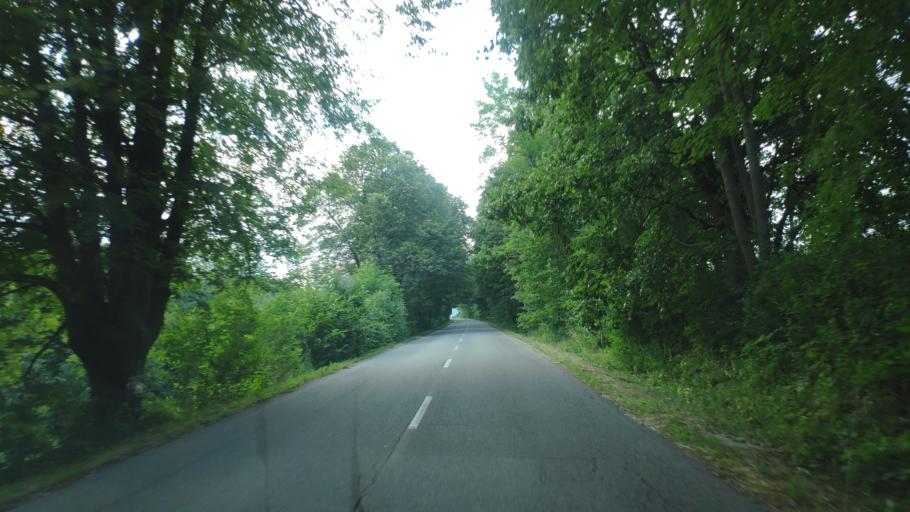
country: SK
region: Kosicky
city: Medzev
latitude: 48.6914
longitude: 20.9739
